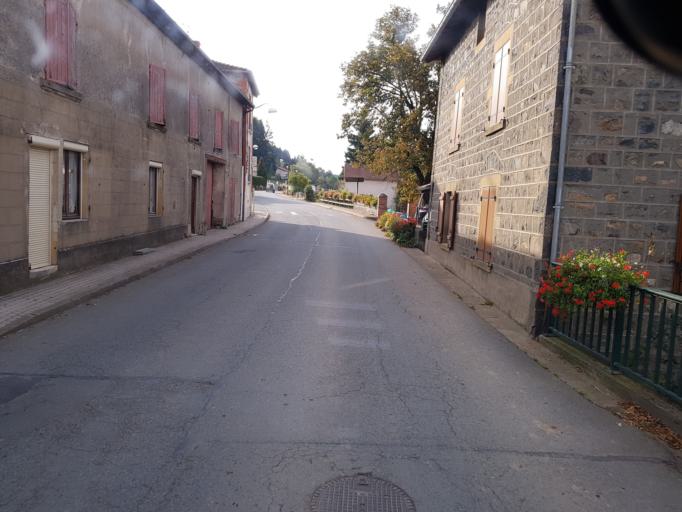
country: FR
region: Rhone-Alpes
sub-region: Departement de la Loire
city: Belmont-de-la-Loire
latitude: 46.1913
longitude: 4.4370
